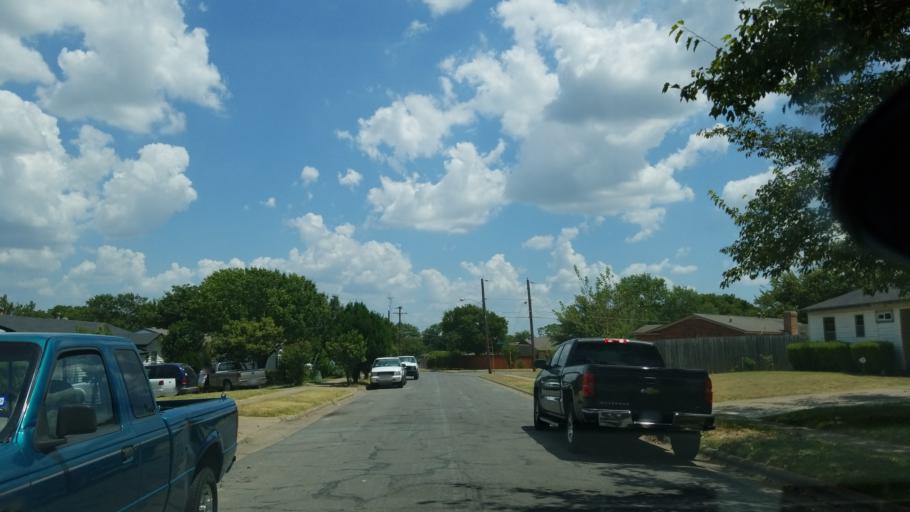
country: US
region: Texas
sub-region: Dallas County
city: Cockrell Hill
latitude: 32.7181
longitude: -96.8949
